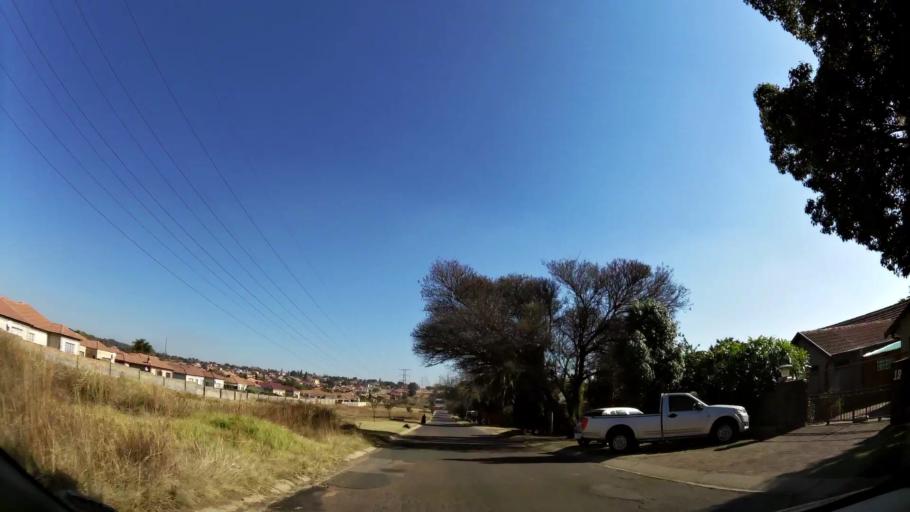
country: ZA
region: Mpumalanga
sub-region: Nkangala District Municipality
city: Witbank
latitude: -25.8604
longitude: 29.2501
